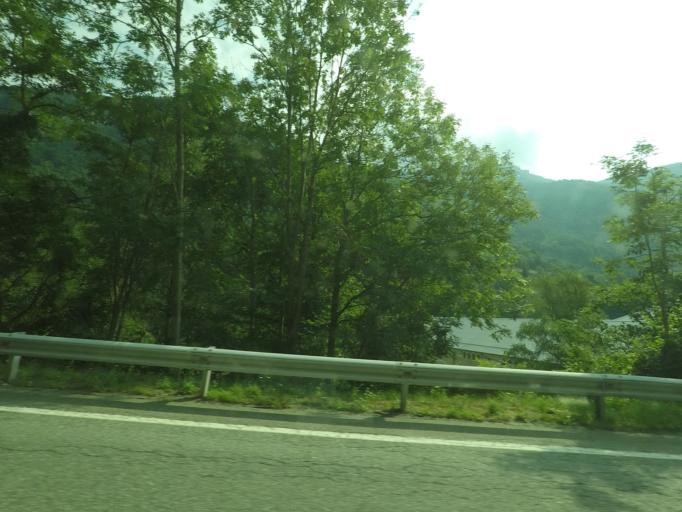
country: IT
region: Aosta Valley
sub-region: Valle d'Aosta
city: Antey-Saint-Andre
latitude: 45.7744
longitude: 7.5940
